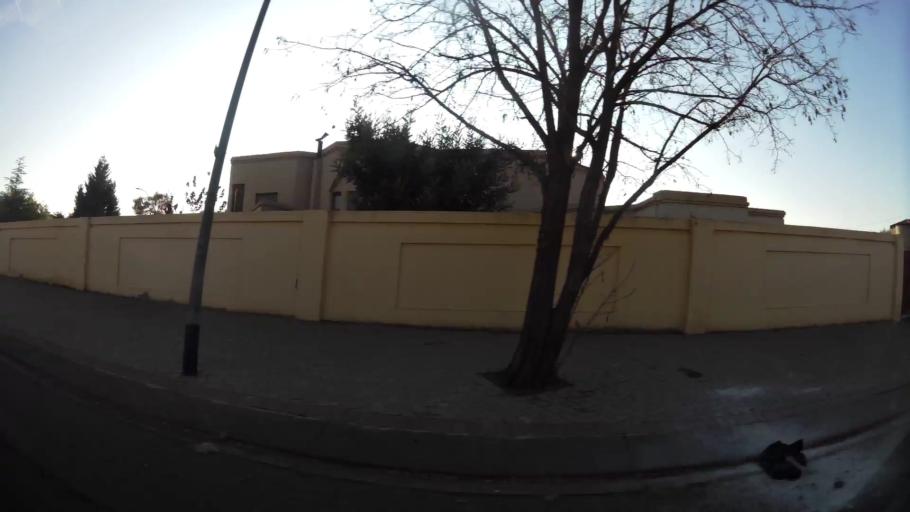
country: ZA
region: Orange Free State
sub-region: Mangaung Metropolitan Municipality
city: Bloemfontein
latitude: -29.1589
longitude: 26.1744
